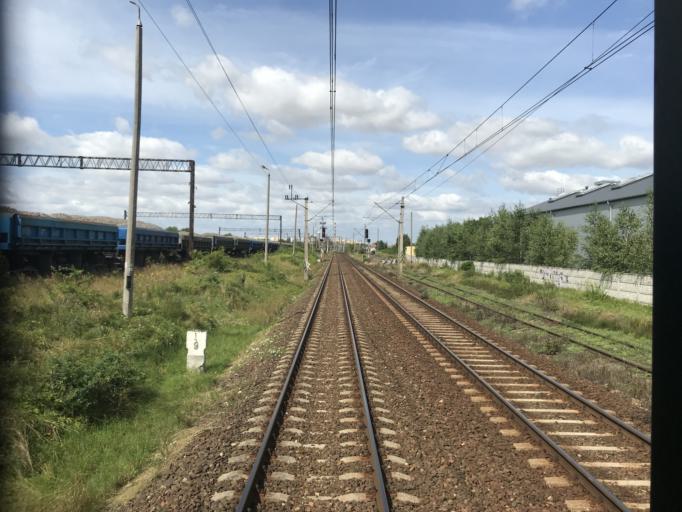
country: PL
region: Pomeranian Voivodeship
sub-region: Powiat malborski
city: Malbork
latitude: 54.0341
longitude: 19.0624
